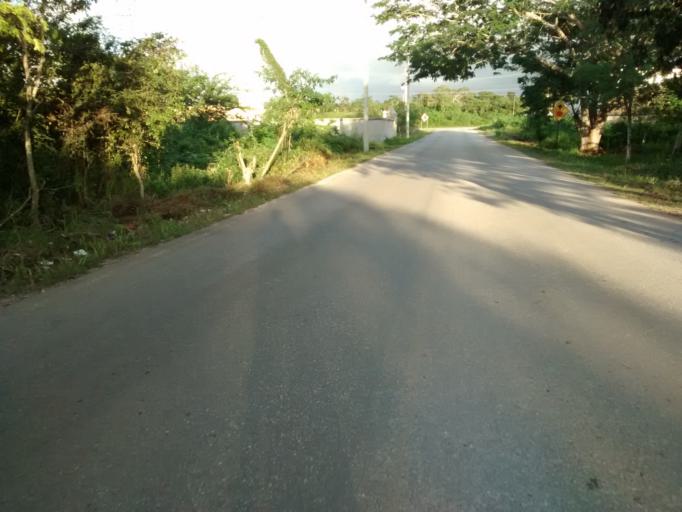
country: MX
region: Yucatan
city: Valladolid
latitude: 20.7311
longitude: -88.2048
